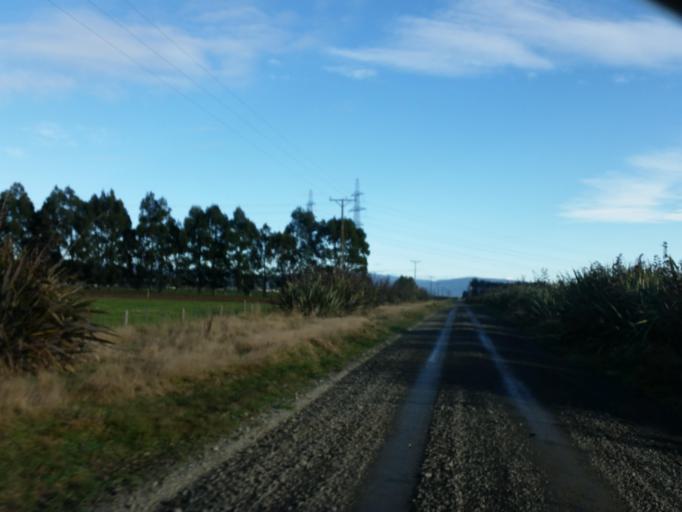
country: NZ
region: Southland
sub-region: Southland District
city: Winton
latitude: -46.1393
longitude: 168.1310
